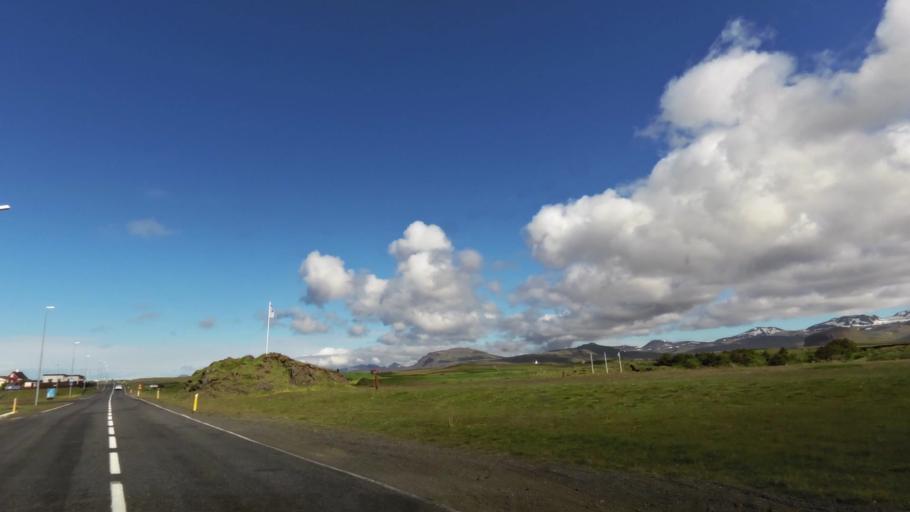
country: IS
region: West
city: Olafsvik
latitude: 64.9150
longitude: -23.8854
